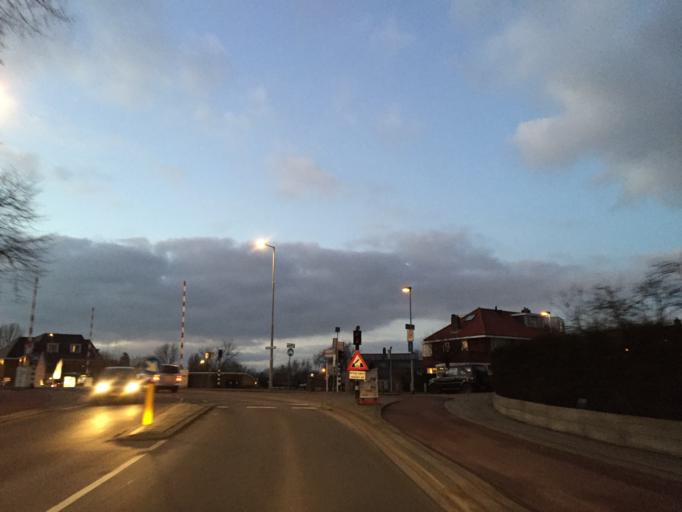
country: NL
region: South Holland
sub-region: Gemeente Lansingerland
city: Bergschenhoek
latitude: 51.9553
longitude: 4.5193
